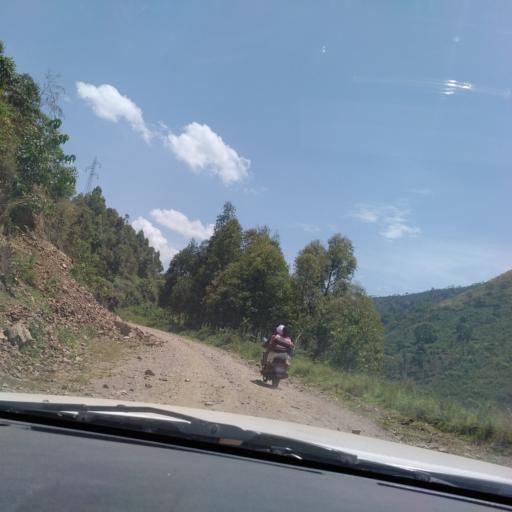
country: CD
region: Nord Kivu
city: Sake
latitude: -1.9744
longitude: 28.9140
